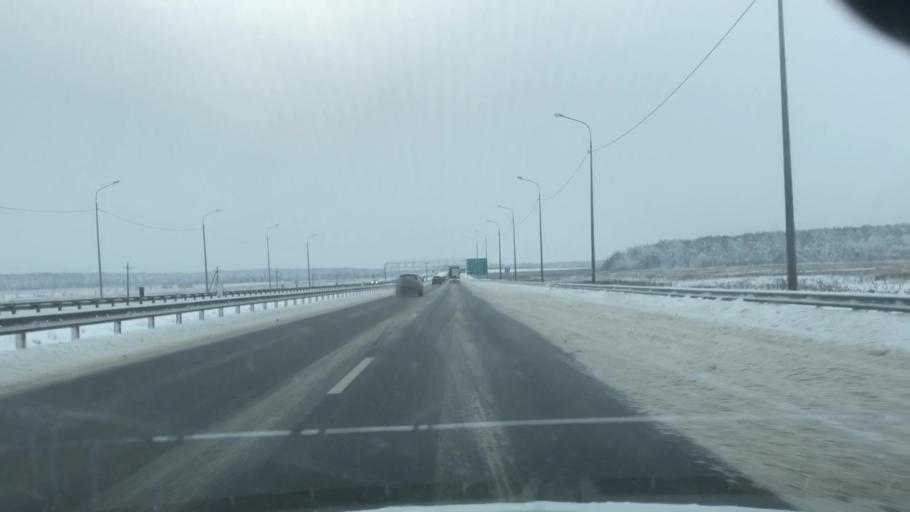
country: RU
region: Moskovskaya
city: Mikhnevo
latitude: 55.0909
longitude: 37.9309
